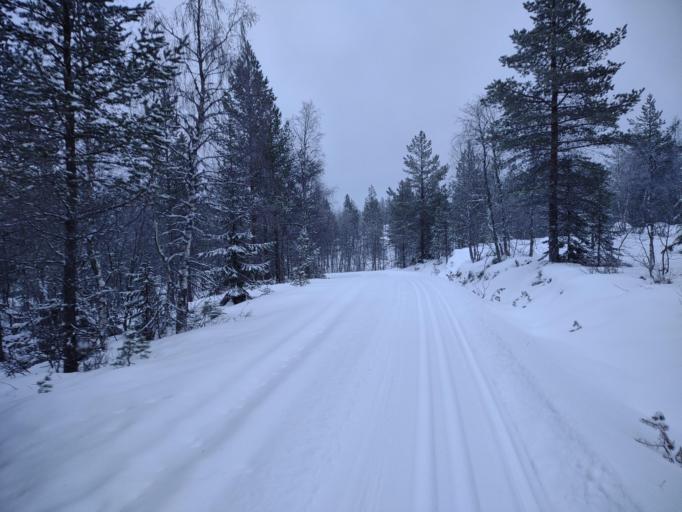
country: NO
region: Buskerud
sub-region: Flesberg
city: Lampeland
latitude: 59.7465
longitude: 9.4911
